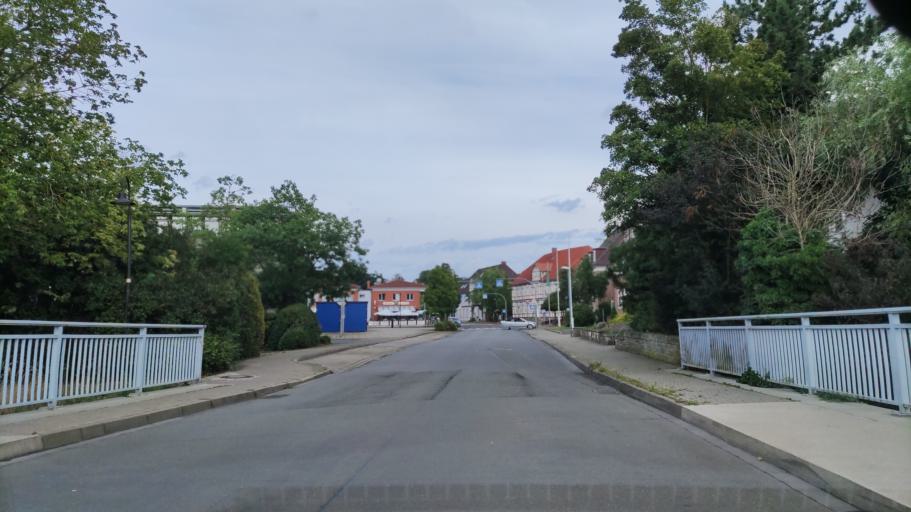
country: DE
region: Lower Saxony
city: Luechow
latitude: 52.9662
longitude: 11.1588
